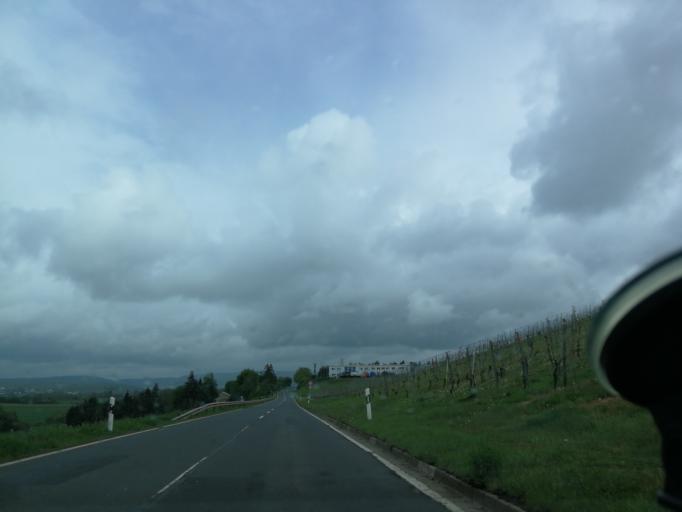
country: DE
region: Rheinland-Pfalz
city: Osann-Monzel
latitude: 49.9332
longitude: 6.9442
